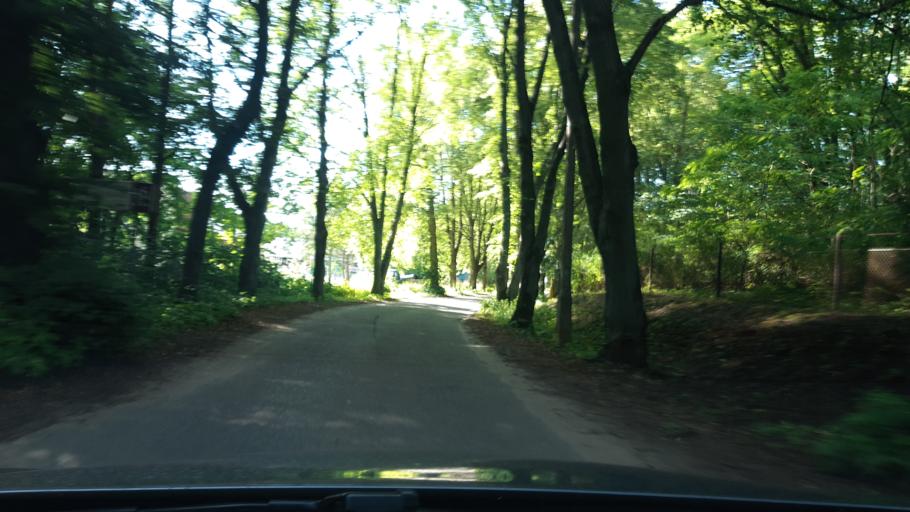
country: PL
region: Warmian-Masurian Voivodeship
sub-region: Powiat mragowski
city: Mragowo
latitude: 53.8733
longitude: 21.3249
